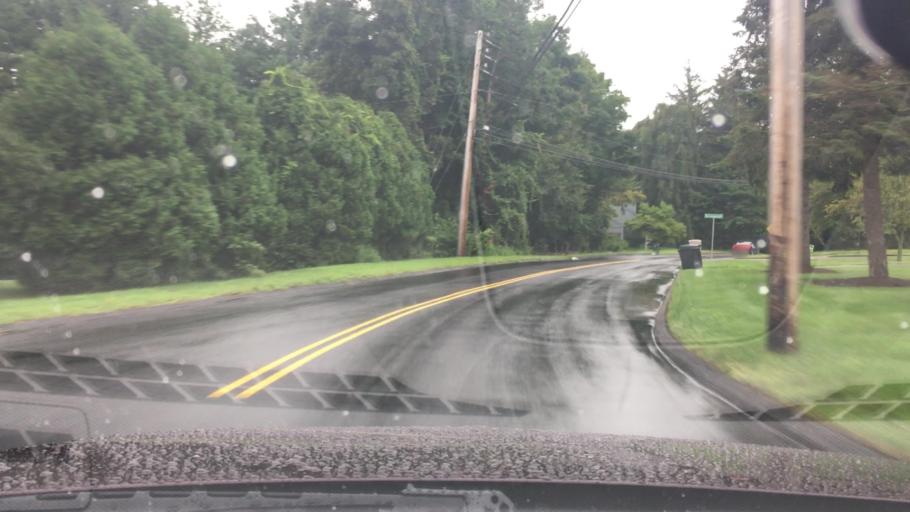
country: US
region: Connecticut
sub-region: New Haven County
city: Cheshire Village
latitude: 41.5265
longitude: -72.9148
